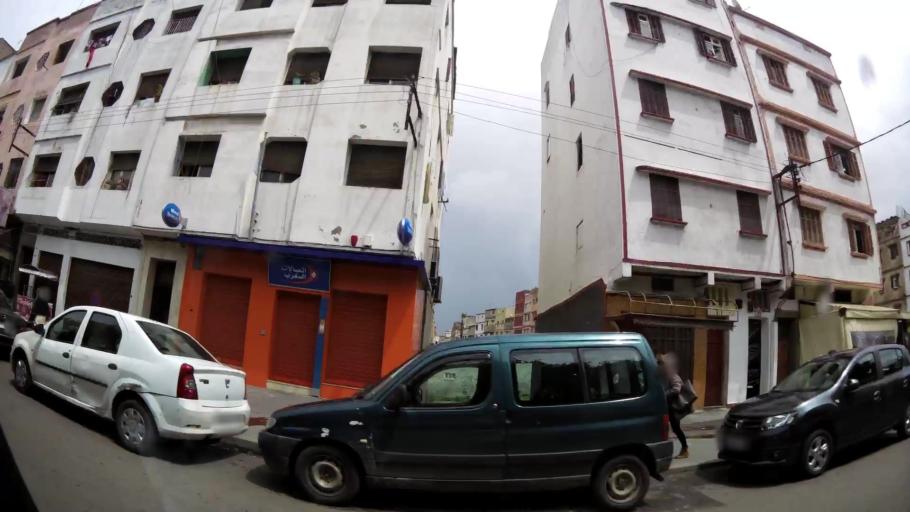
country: MA
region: Grand Casablanca
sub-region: Casablanca
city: Casablanca
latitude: 33.5689
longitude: -7.5916
